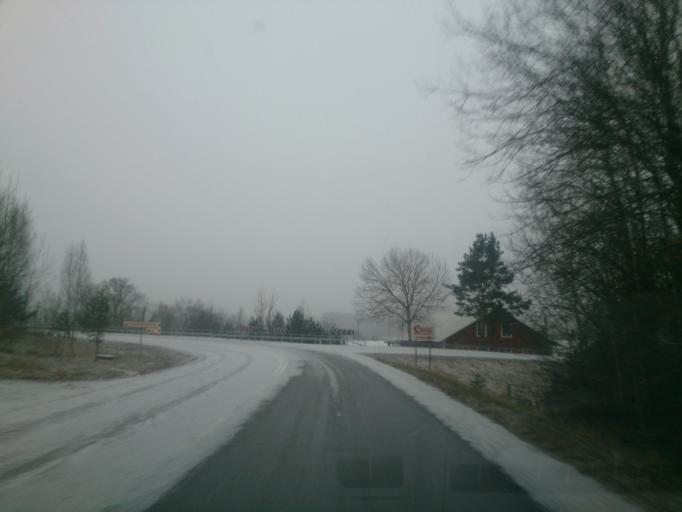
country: SE
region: OEstergoetland
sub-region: Soderkopings Kommun
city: Soederkoeping
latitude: 58.4926
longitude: 16.3069
